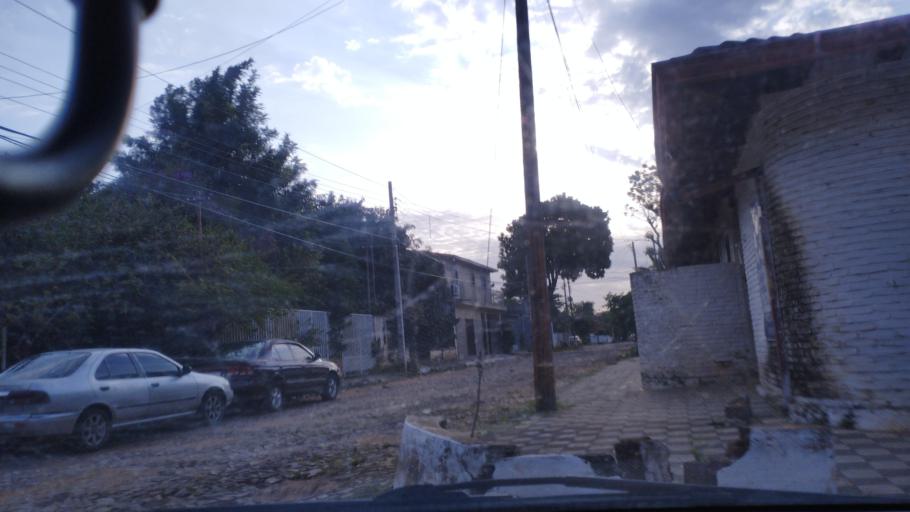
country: PY
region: Central
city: Fernando de la Mora
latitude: -25.3116
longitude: -57.5380
